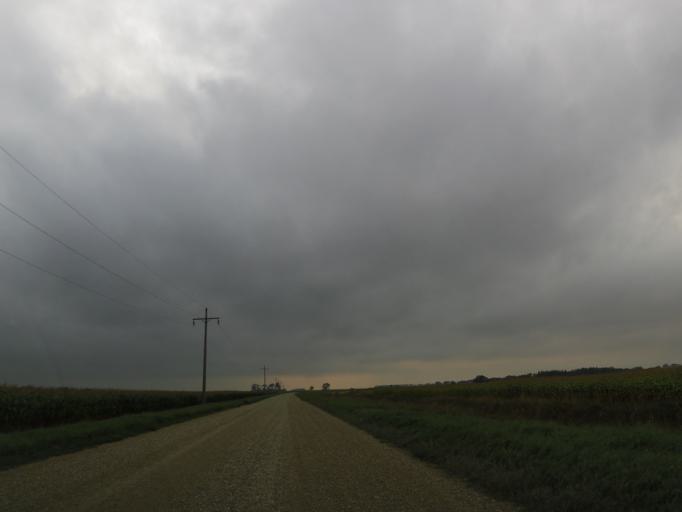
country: US
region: North Dakota
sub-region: Walsh County
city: Grafton
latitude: 48.5285
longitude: -97.1717
